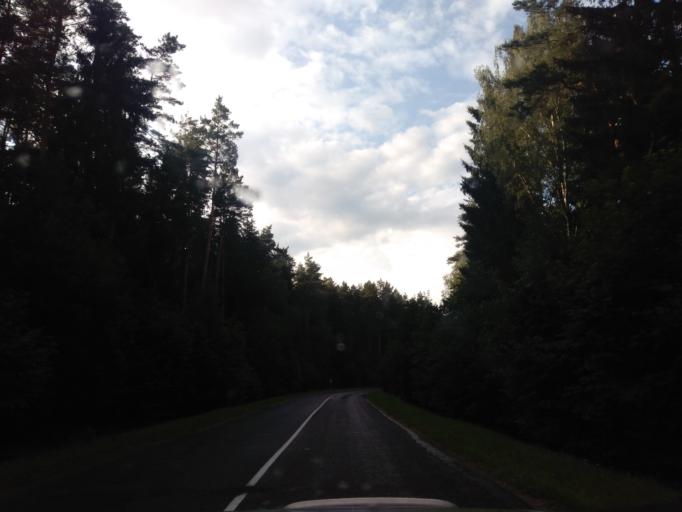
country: BY
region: Minsk
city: Kapyl'
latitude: 53.2716
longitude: 27.0757
